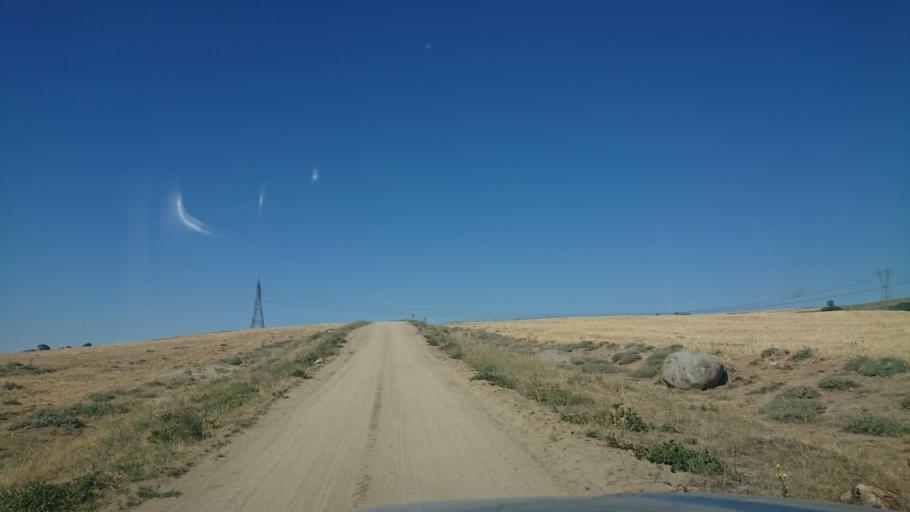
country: TR
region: Aksaray
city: Sariyahsi
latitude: 38.9413
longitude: 33.8721
